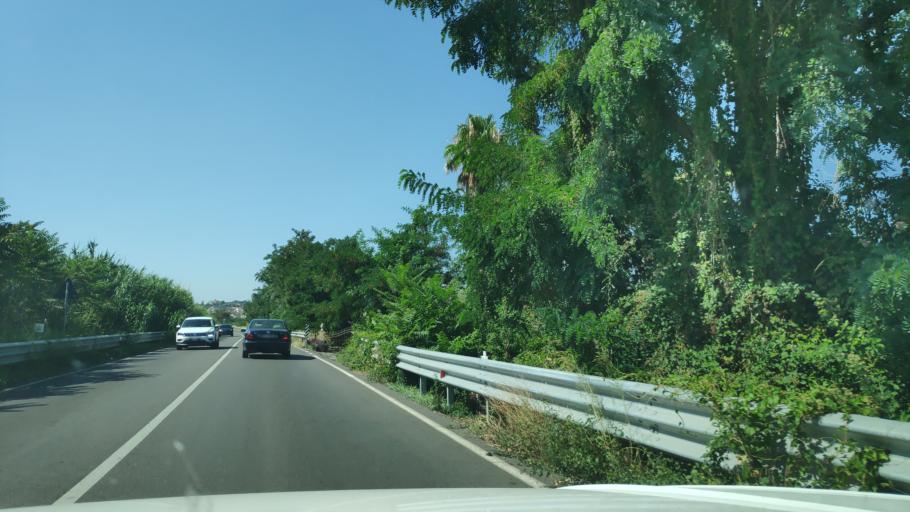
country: IT
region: Calabria
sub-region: Provincia di Reggio Calabria
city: Bovalino
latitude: 38.1314
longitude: 16.1606
